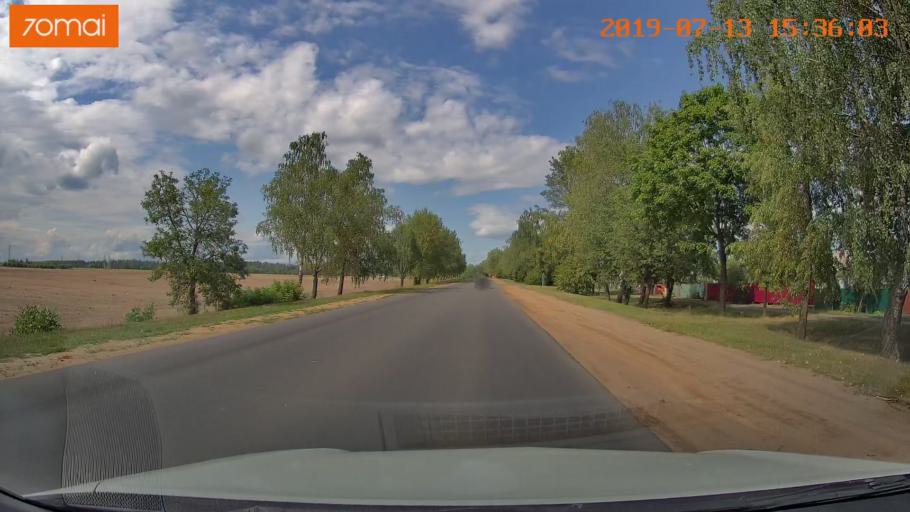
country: BY
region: Mogilev
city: Babruysk
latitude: 53.1279
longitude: 29.1667
